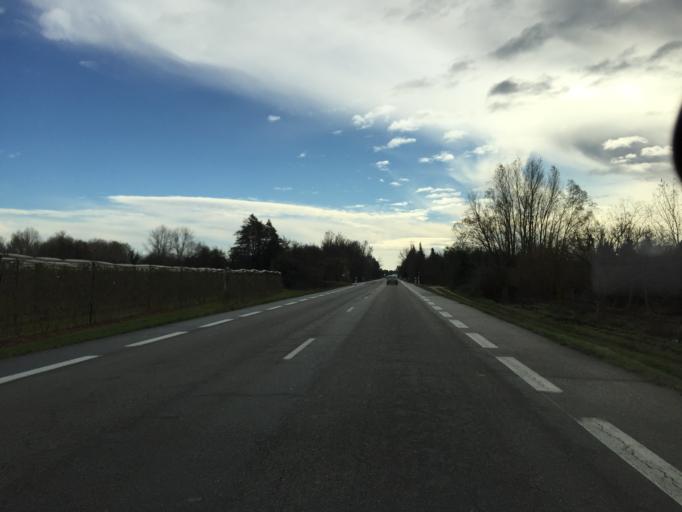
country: FR
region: Provence-Alpes-Cote d'Azur
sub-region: Departement du Vaucluse
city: Velleron
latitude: 43.9406
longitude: 5.0289
